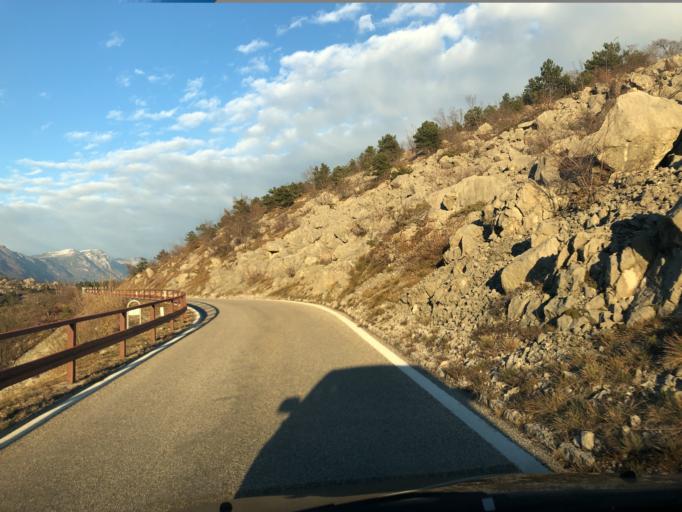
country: IT
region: Trentino-Alto Adige
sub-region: Provincia di Trento
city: Drena
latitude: 45.9789
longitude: 10.9377
